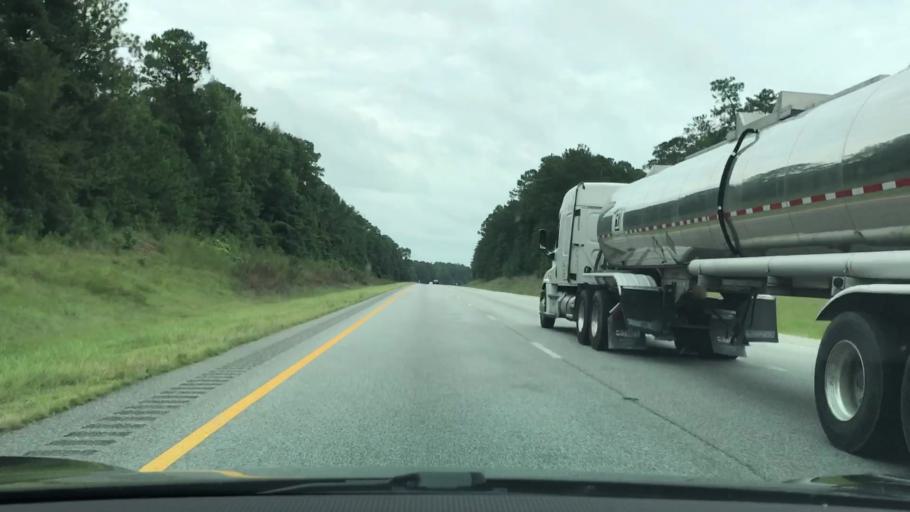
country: US
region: Alabama
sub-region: Macon County
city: Tuskegee
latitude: 32.5022
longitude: -85.6106
